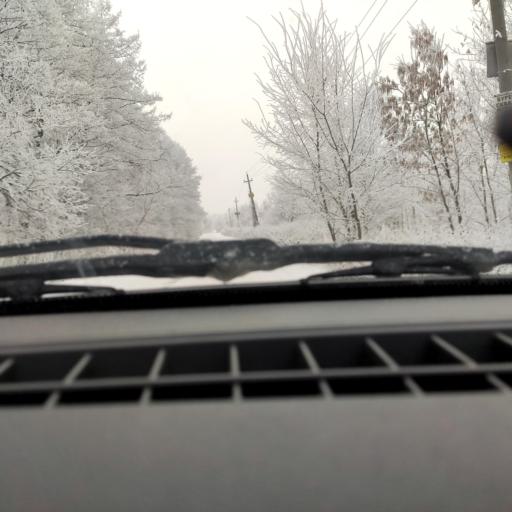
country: RU
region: Bashkortostan
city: Ufa
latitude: 54.7108
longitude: 56.1276
